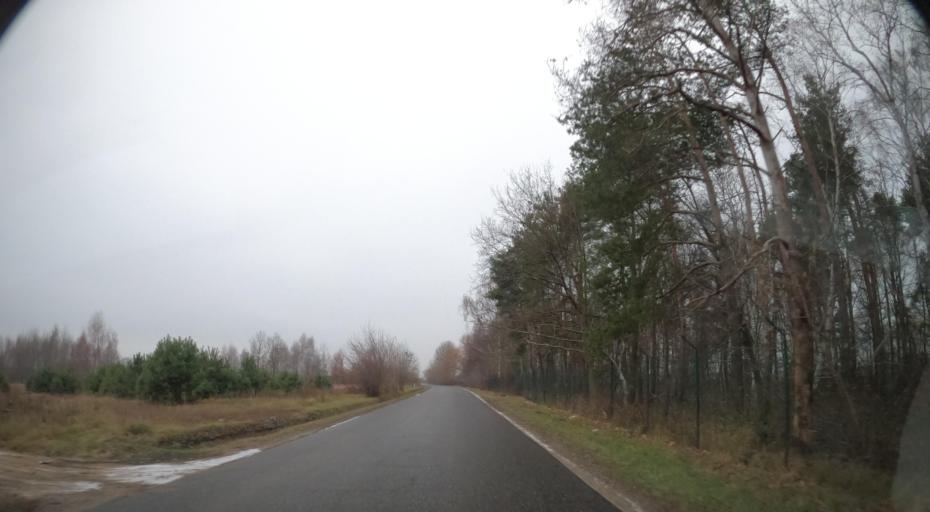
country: PL
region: Masovian Voivodeship
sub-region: Radom
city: Radom
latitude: 51.3834
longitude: 21.2131
